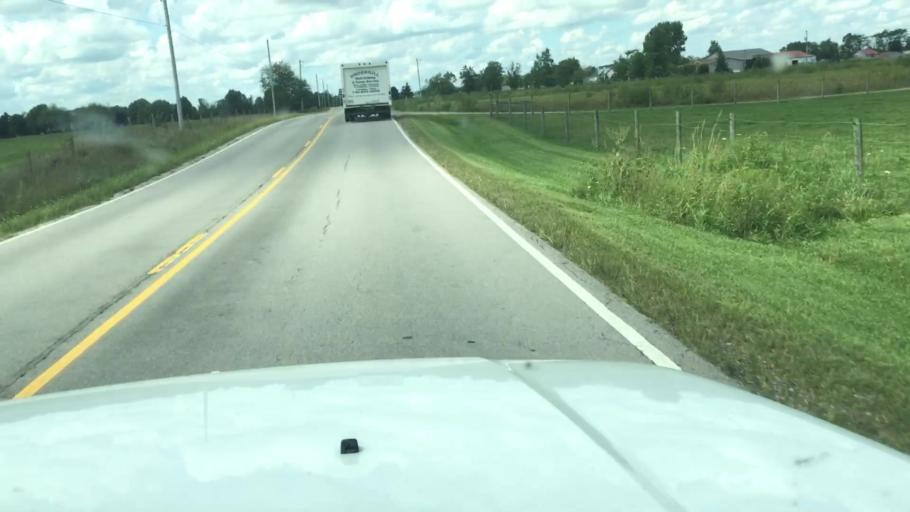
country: US
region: Ohio
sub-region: Madison County
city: London
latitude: 39.8288
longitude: -83.3666
